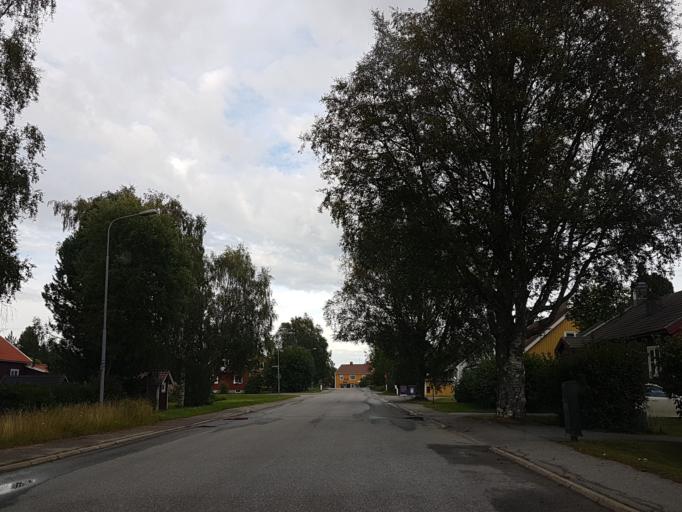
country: SE
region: Vaesterbotten
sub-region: Umea Kommun
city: Saevar
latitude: 63.8996
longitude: 20.5463
